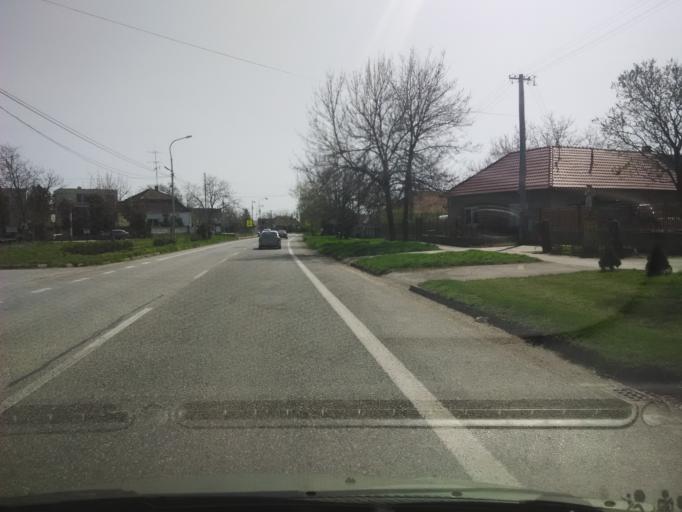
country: SK
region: Nitriansky
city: Surany
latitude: 48.0922
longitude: 18.0663
